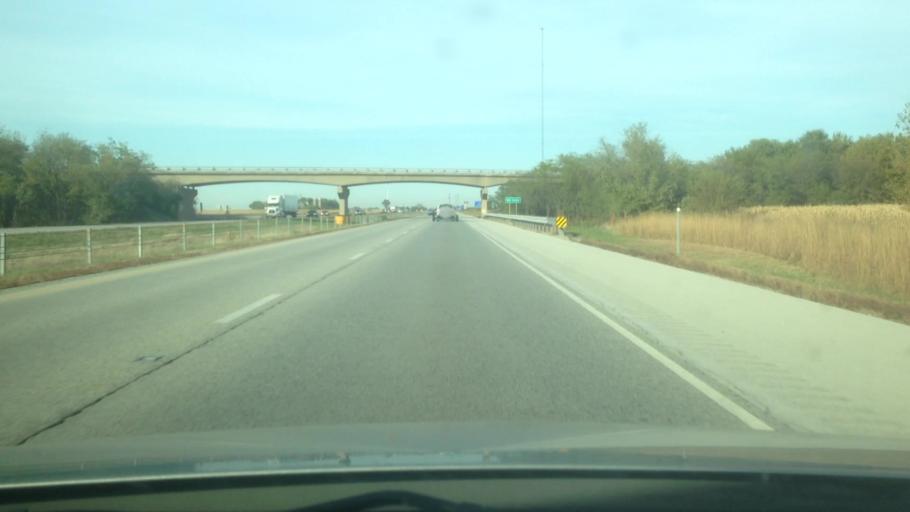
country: US
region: Illinois
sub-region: Kankakee County
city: Manteno
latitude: 41.2940
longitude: -87.8311
